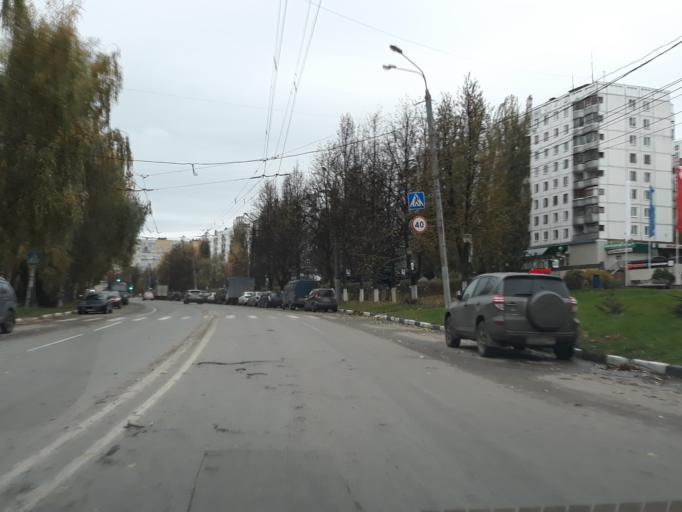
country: RU
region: Nizjnij Novgorod
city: Afonino
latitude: 56.2833
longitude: 44.0455
